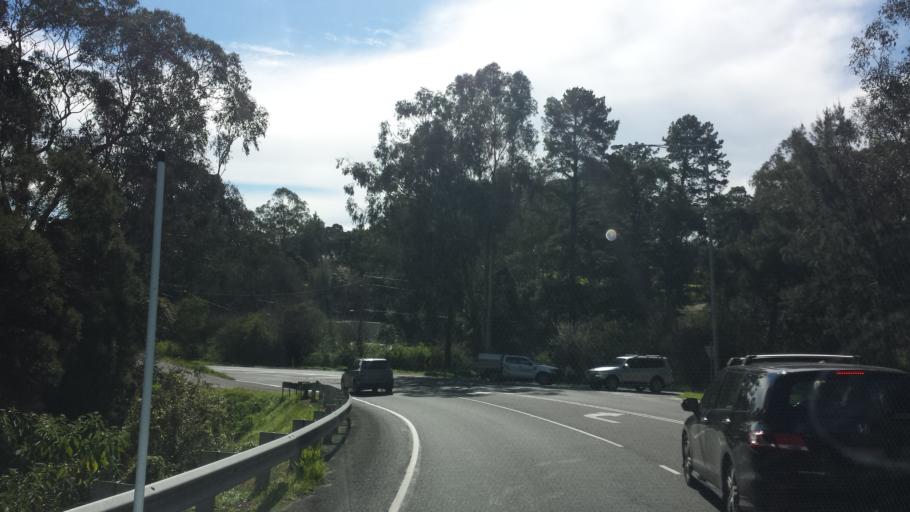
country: AU
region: Victoria
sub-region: Maroondah
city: Warranwood
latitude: -37.7744
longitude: 145.2317
